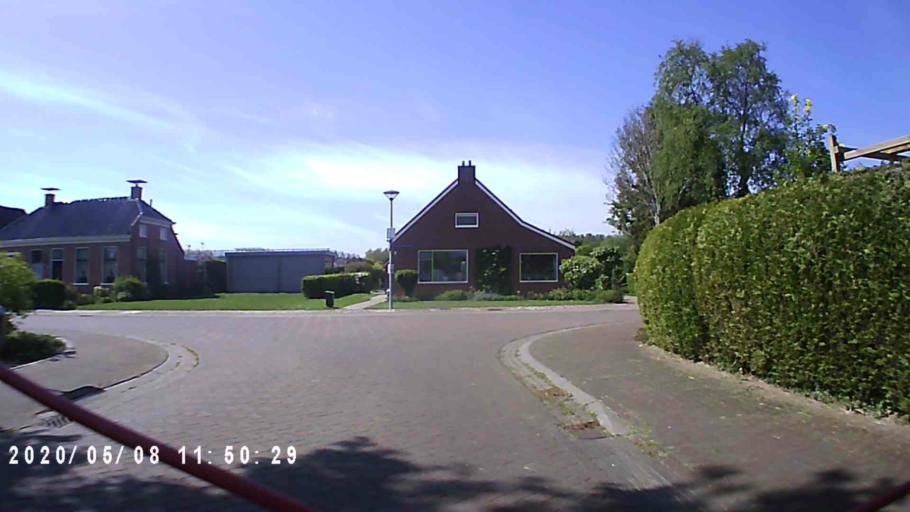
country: NL
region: Groningen
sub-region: Gemeente Bedum
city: Bedum
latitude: 53.3211
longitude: 6.6937
